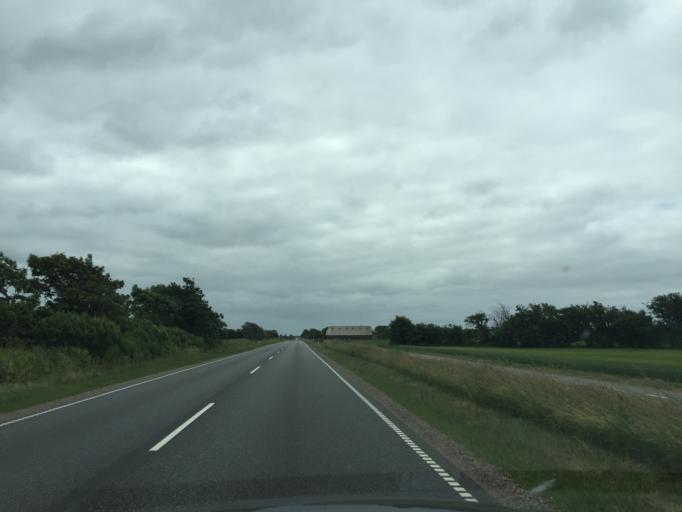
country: DK
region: South Denmark
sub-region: Tonder Kommune
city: Sherrebek
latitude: 55.2274
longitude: 8.7247
